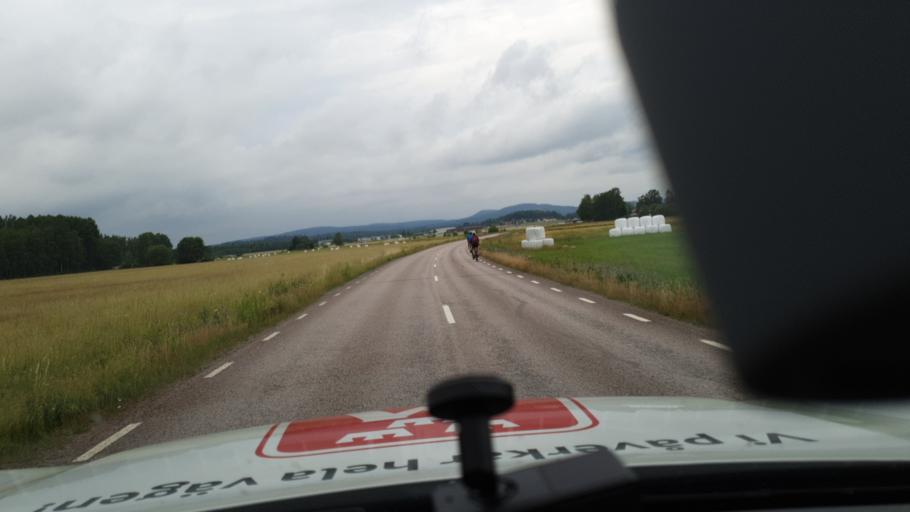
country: SE
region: Vaermland
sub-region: Sunne Kommun
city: Sunne
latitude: 59.8298
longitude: 13.1821
